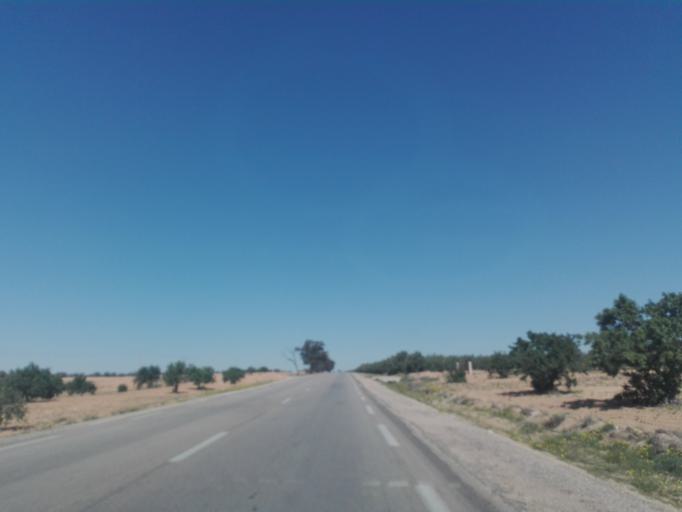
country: TN
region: Safaqis
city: Bi'r `Ali Bin Khalifah
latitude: 34.7482
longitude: 10.3525
